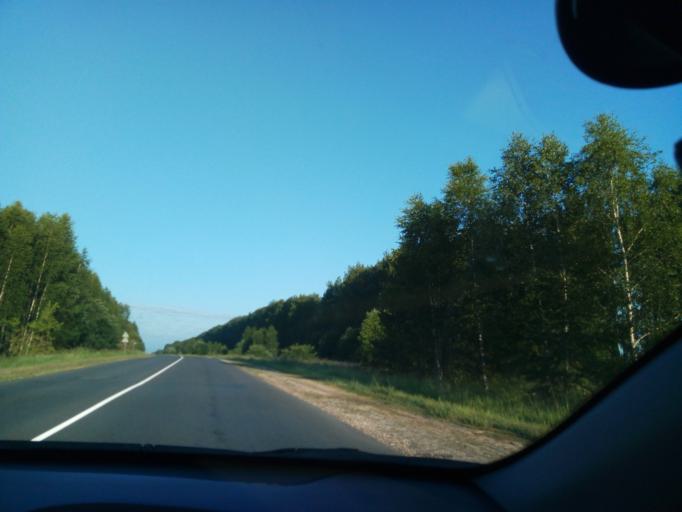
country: RU
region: Nizjnij Novgorod
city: Satis
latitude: 54.9007
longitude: 43.1358
